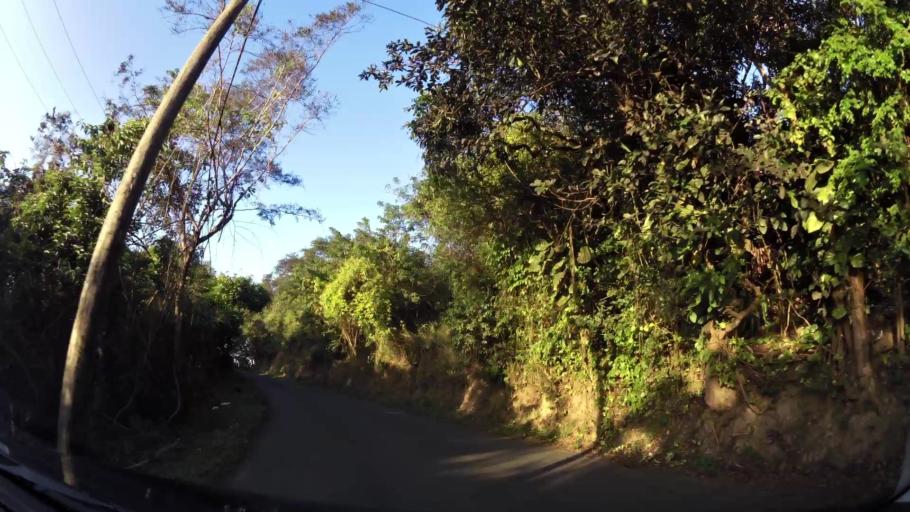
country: VG
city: Road Town
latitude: 18.4393
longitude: -64.6190
